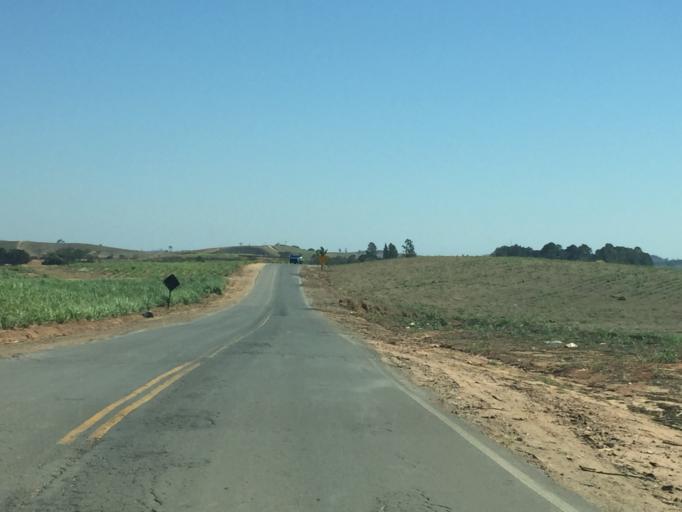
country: BR
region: Sao Paulo
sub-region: Itapira
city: Itapira
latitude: -22.4163
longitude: -46.7972
